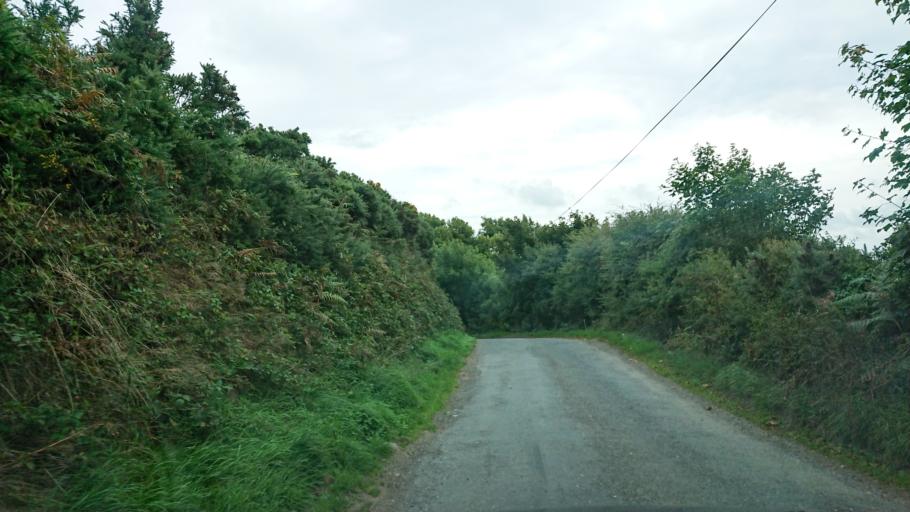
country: IE
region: Munster
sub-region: Waterford
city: Dunmore East
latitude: 52.1813
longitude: -7.0015
